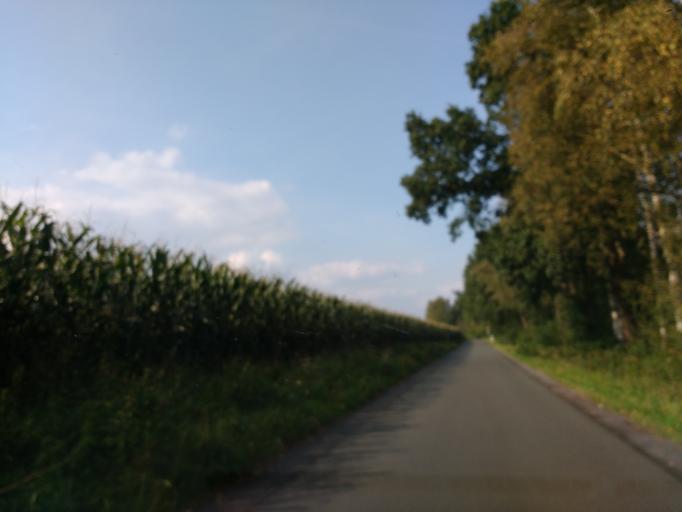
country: DE
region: North Rhine-Westphalia
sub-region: Regierungsbezirk Detmold
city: Hovelhof
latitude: 51.7857
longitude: 8.7010
